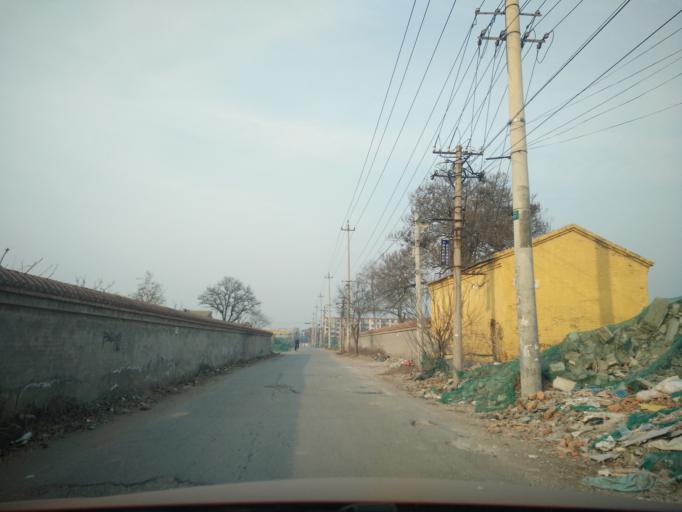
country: CN
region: Beijing
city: Jiugong
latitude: 39.7982
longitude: 116.4250
